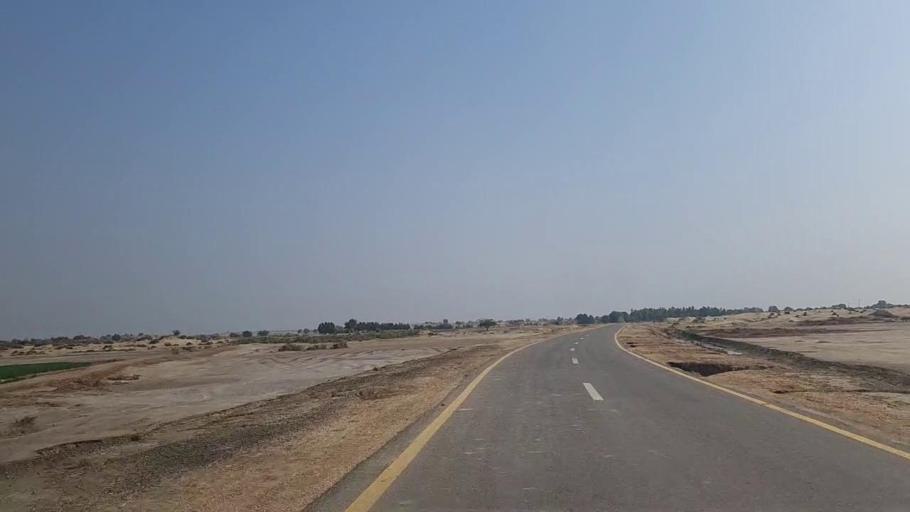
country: PK
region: Sindh
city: Jam Sahib
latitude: 26.3720
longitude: 68.5325
